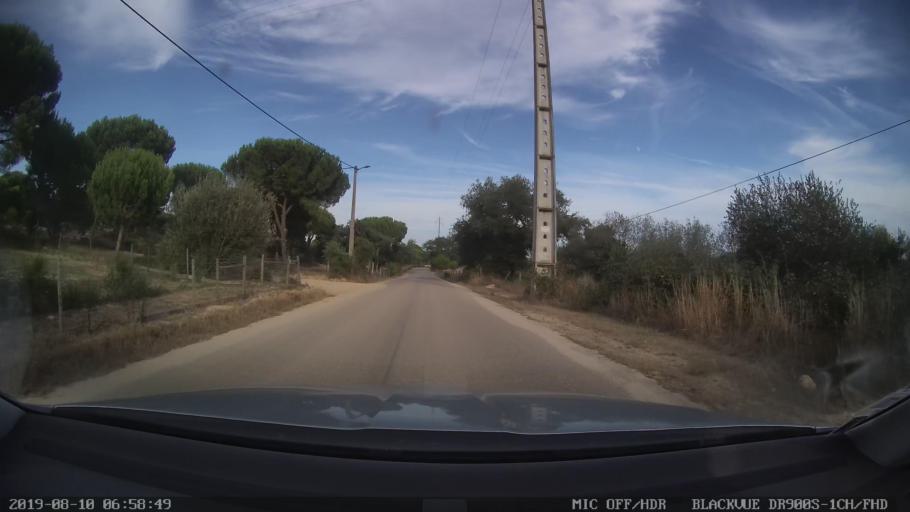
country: PT
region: Santarem
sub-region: Benavente
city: Poceirao
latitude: 38.8473
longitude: -8.7126
